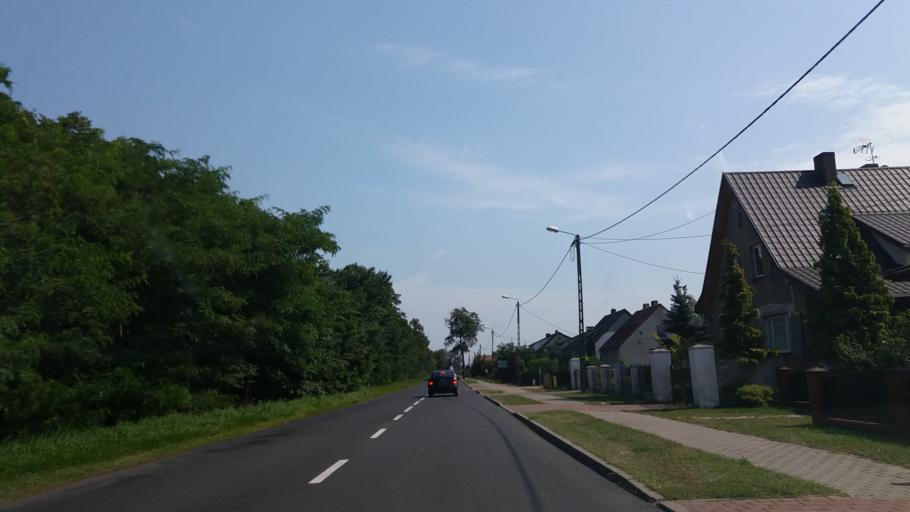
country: PL
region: Lubusz
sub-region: Powiat strzelecko-drezdenecki
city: Zwierzyn
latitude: 52.8392
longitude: 15.5715
